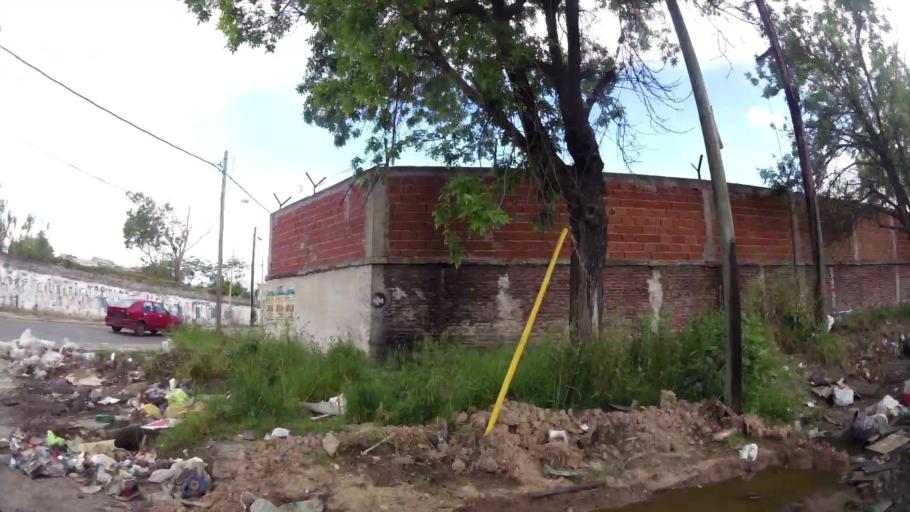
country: AR
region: Buenos Aires
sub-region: Partido de Lanus
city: Lanus
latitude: -34.6989
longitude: -58.3662
